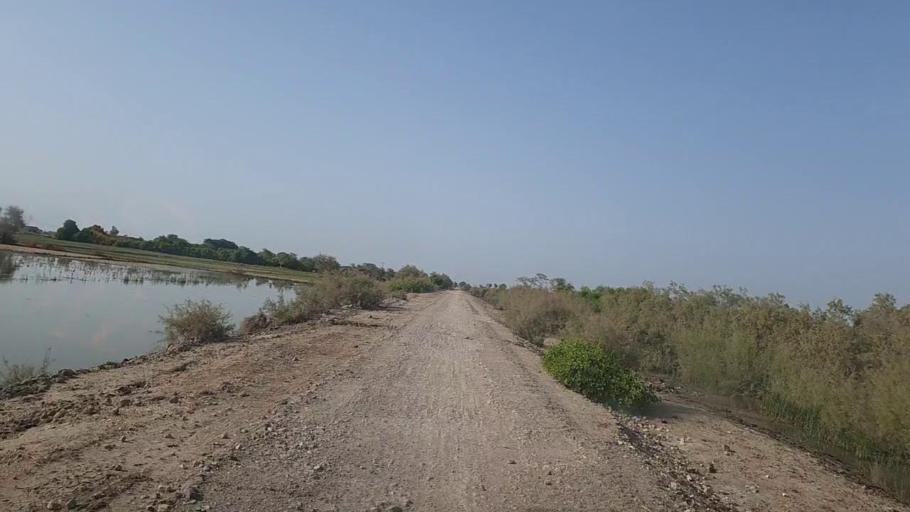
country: PK
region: Sindh
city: Sita Road
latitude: 27.0992
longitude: 67.8735
